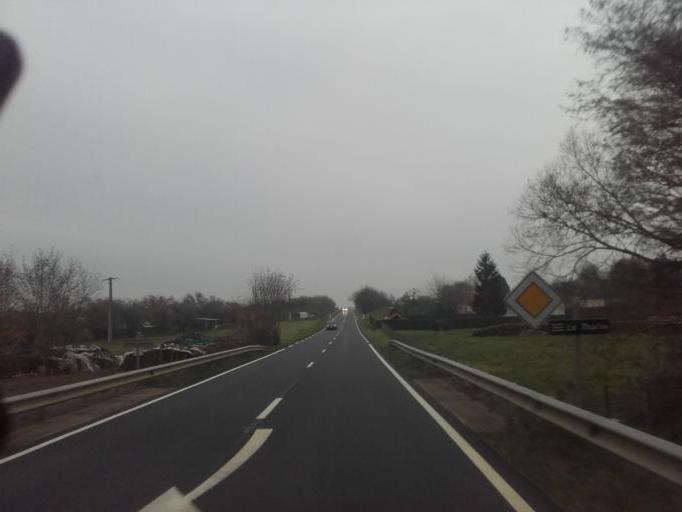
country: FR
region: Bourgogne
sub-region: Departement de Saone-et-Loire
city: Rully
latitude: 46.8769
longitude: 4.7524
